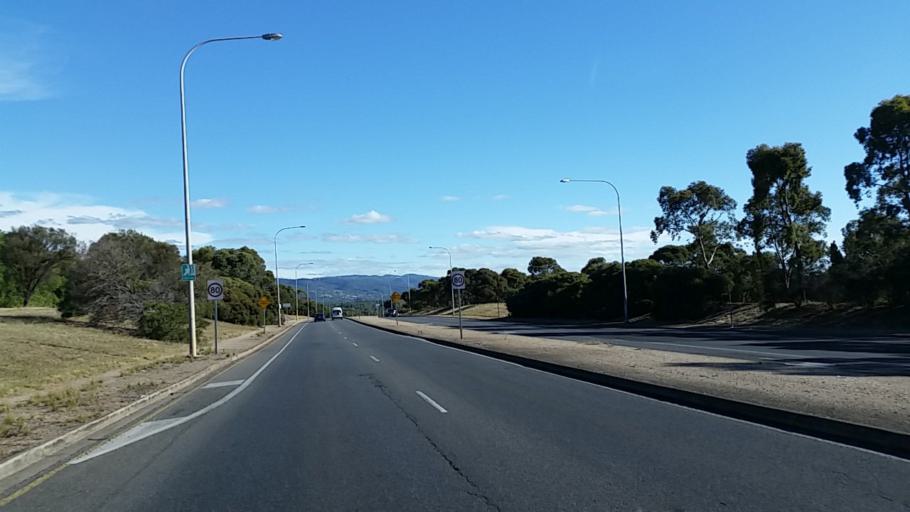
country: AU
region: South Australia
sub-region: Tea Tree Gully
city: Modbury
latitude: -34.8184
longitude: 138.6775
